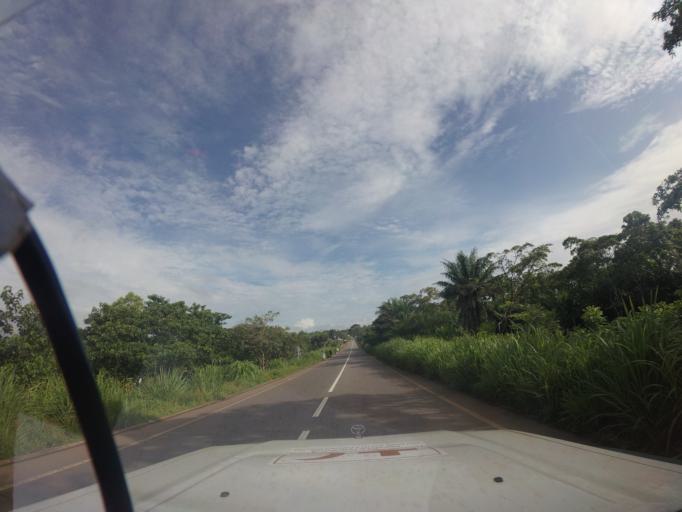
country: SL
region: Northern Province
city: Kambia
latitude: 9.1168
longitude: -12.9301
